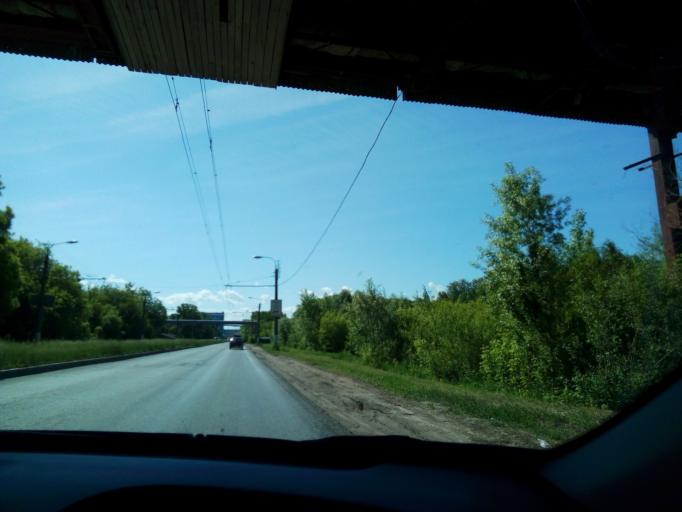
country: RU
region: Chuvashia
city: Novocheboksarsk
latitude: 56.0830
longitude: 47.5045
